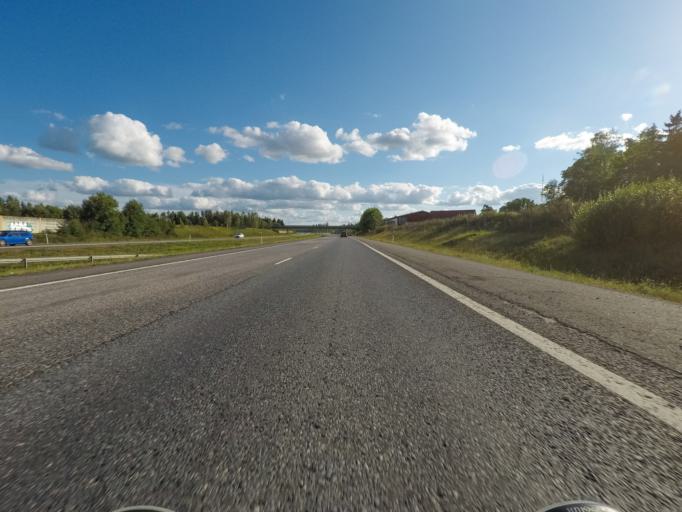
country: FI
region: Uusimaa
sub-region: Helsinki
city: Jaervenpaeae
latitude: 60.5096
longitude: 25.1391
